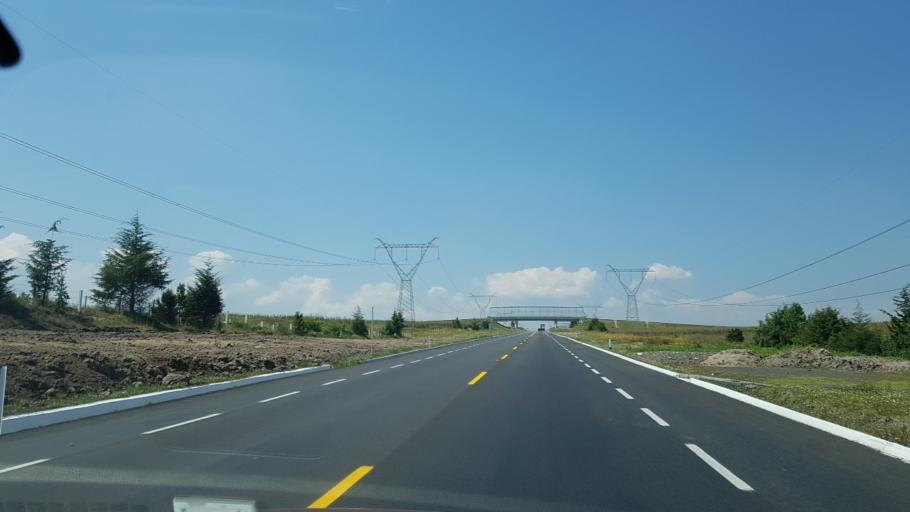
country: MX
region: Mexico
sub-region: Almoloya de Juarez
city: Conjunto Habitacional Ecologico SUTEYM
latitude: 19.3838
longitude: -99.7780
